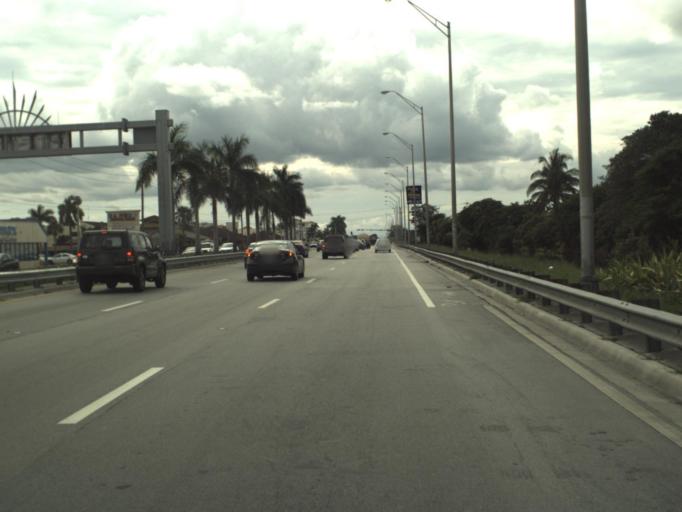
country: US
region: Florida
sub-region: Miami-Dade County
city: Flagami
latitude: 25.7624
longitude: -80.3242
